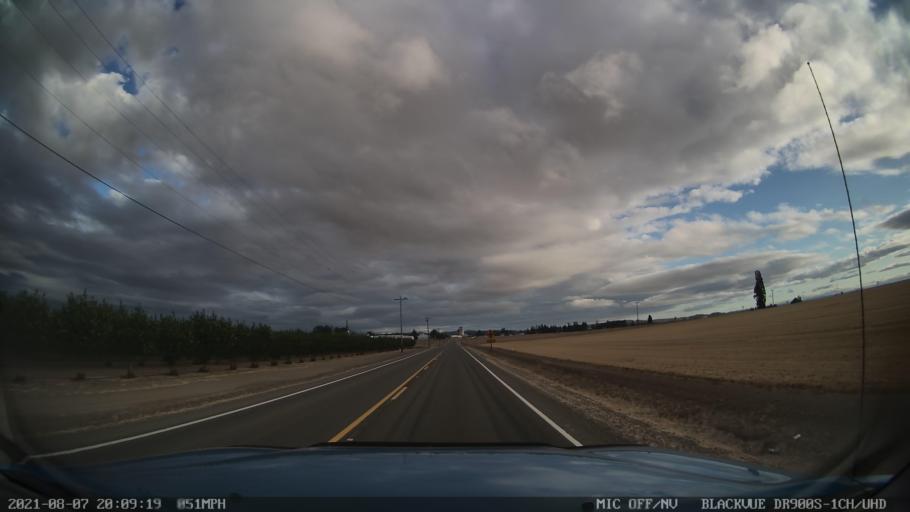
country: US
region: Oregon
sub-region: Marion County
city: Silverton
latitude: 44.9725
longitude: -122.8775
